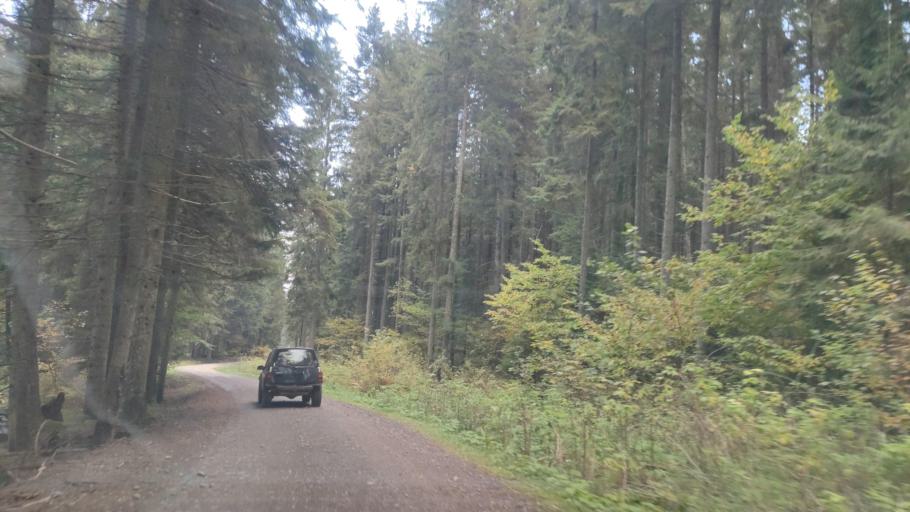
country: RO
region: Harghita
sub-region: Comuna Madaras
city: Madaras
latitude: 46.4833
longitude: 25.6666
